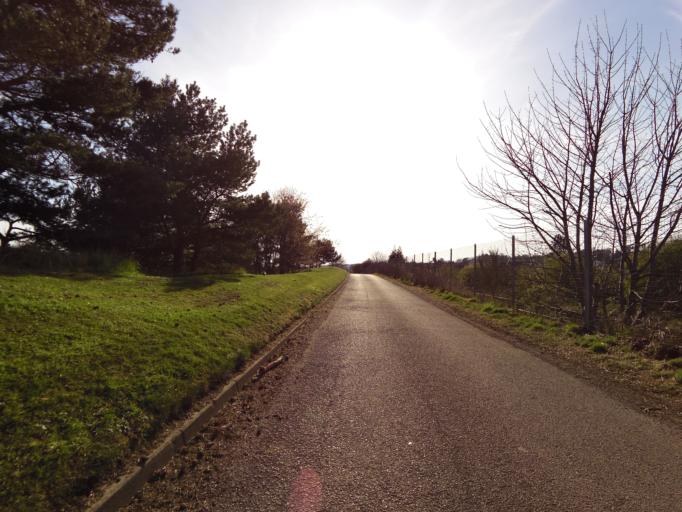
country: GB
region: Scotland
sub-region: Fife
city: Tayport
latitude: 56.4810
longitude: -2.8109
